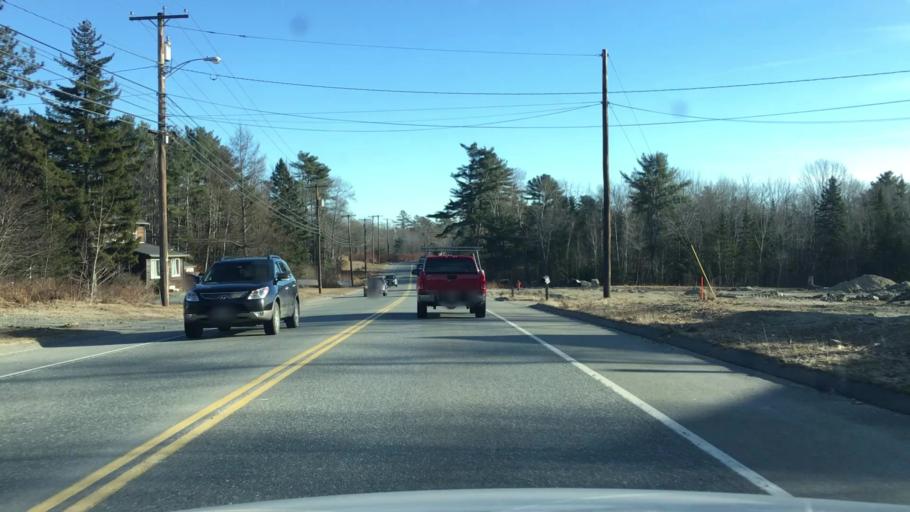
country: US
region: Maine
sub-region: Hancock County
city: Ellsworth
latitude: 44.5665
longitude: -68.4483
